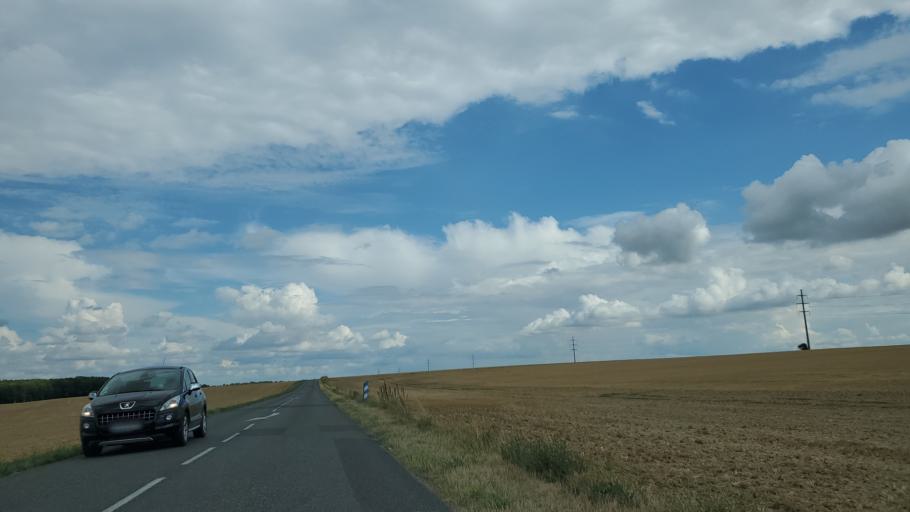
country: FR
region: Ile-de-France
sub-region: Departement de Seine-et-Marne
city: Chailly-en-Brie
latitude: 48.7868
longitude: 3.1358
